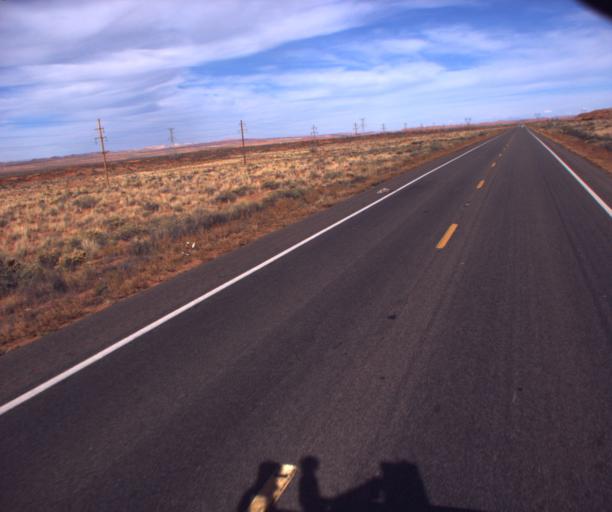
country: US
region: Arizona
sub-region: Navajo County
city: Kayenta
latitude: 36.7942
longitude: -109.9404
